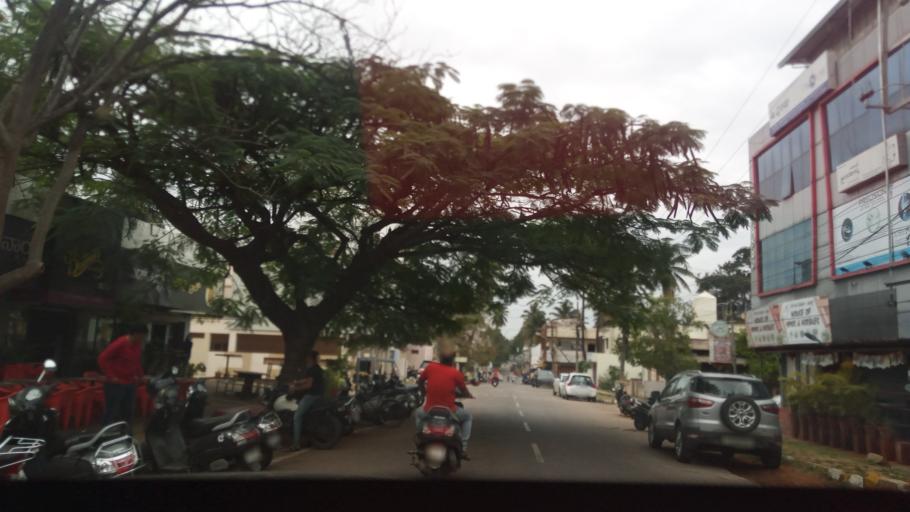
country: IN
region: Karnataka
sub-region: Mysore
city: Mysore
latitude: 12.3025
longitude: 76.6300
